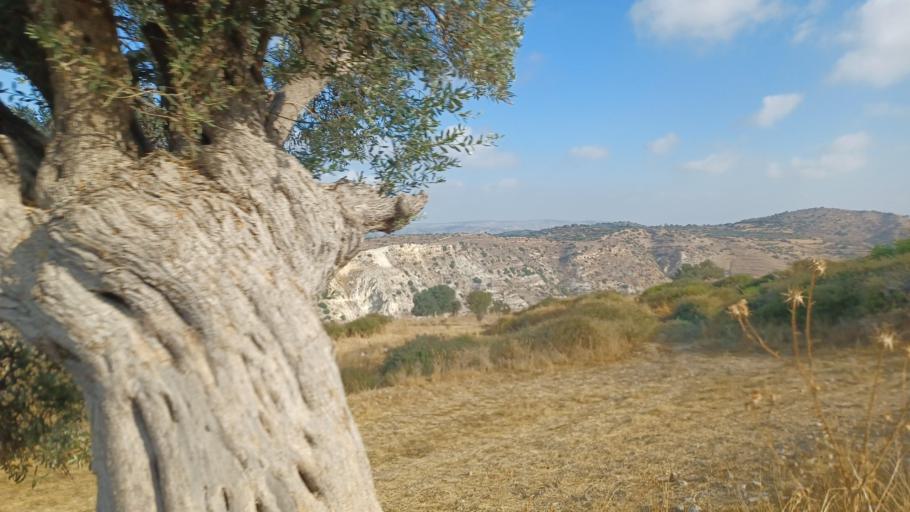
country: CY
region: Pafos
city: Mesogi
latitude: 34.8566
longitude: 32.5839
